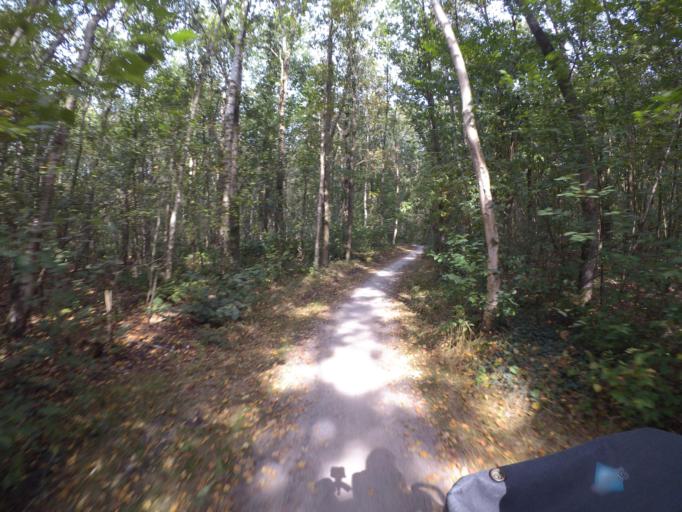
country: NL
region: Drenthe
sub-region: Gemeente Westerveld
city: Havelte
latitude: 52.8273
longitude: 6.2726
